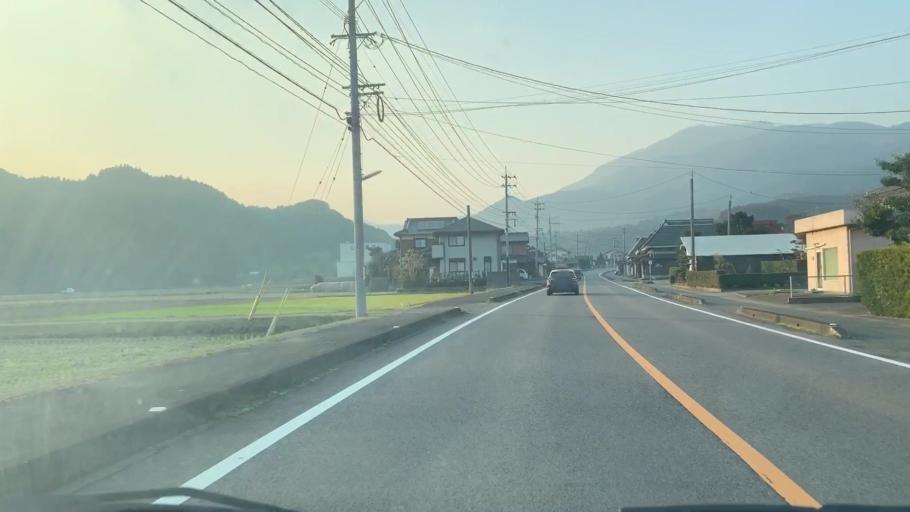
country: JP
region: Saga Prefecture
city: Takeocho-takeo
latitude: 33.2603
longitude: 130.0617
